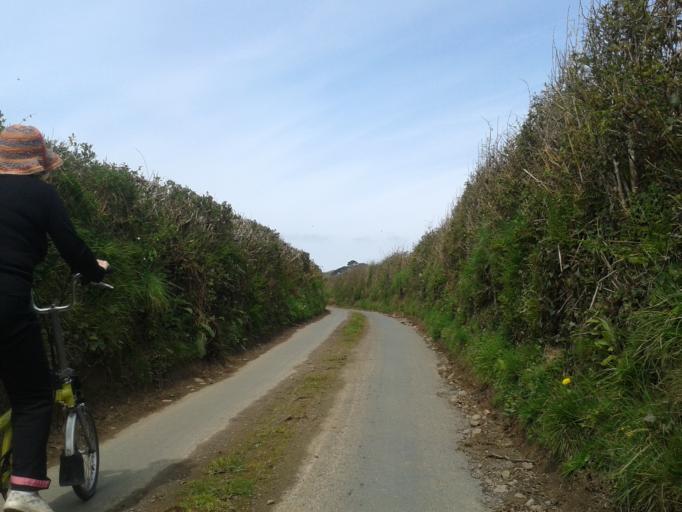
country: GB
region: England
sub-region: Devon
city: Braunton
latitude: 51.1409
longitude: -4.1845
